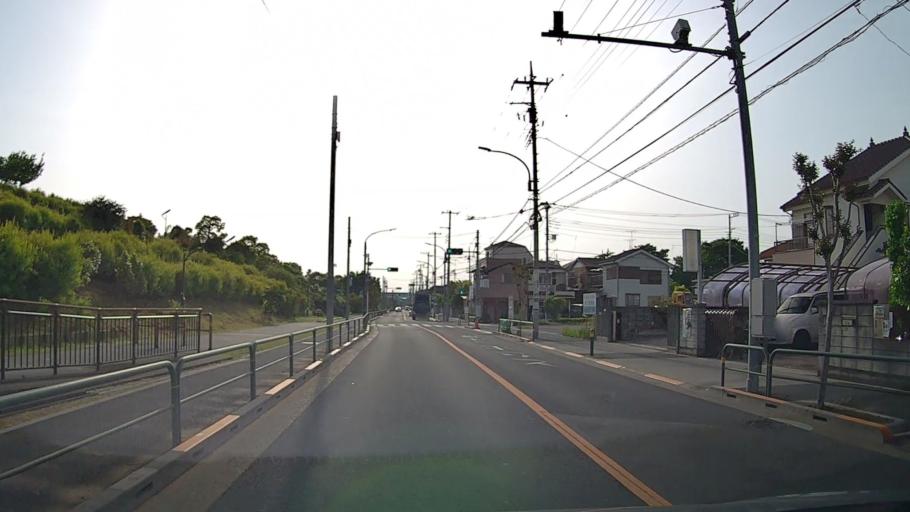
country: JP
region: Saitama
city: Soka
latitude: 35.8011
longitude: 139.7760
